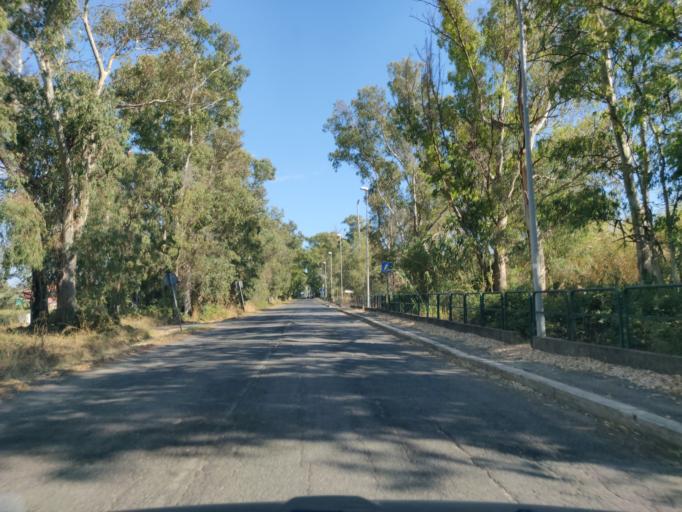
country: IT
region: Latium
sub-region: Citta metropolitana di Roma Capitale
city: Aurelia
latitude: 42.1472
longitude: 11.7613
